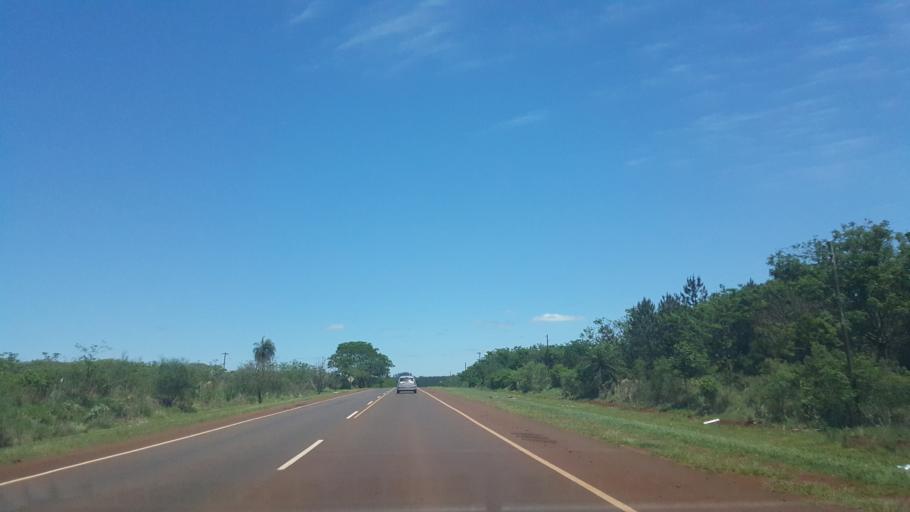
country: AR
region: Misiones
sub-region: Departamento de Capital
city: Posadas
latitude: -27.4244
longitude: -55.9982
